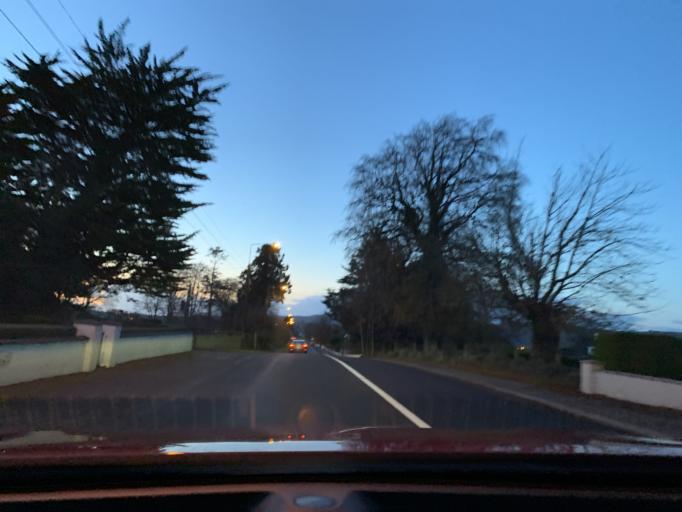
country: IE
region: Connaught
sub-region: Roscommon
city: Boyle
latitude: 53.9702
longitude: -8.2811
